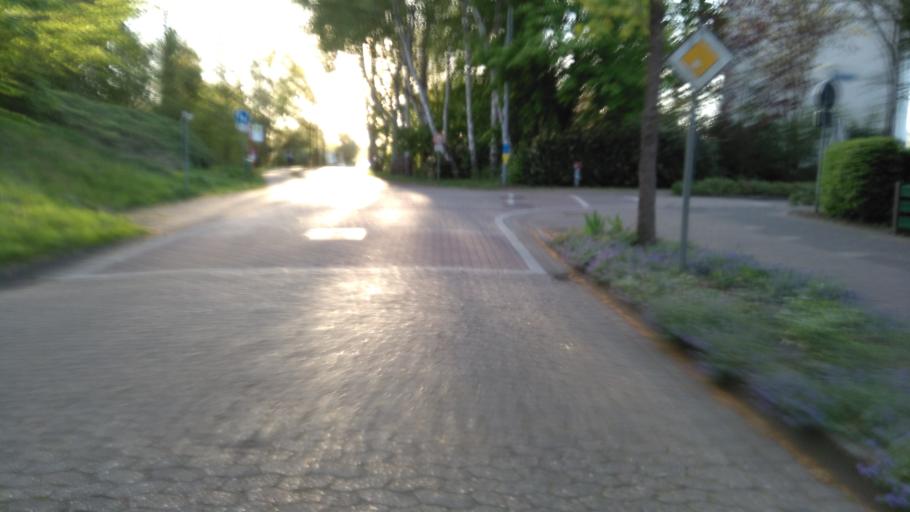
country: DE
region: Lower Saxony
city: Buxtehude
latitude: 53.4719
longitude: 9.6801
